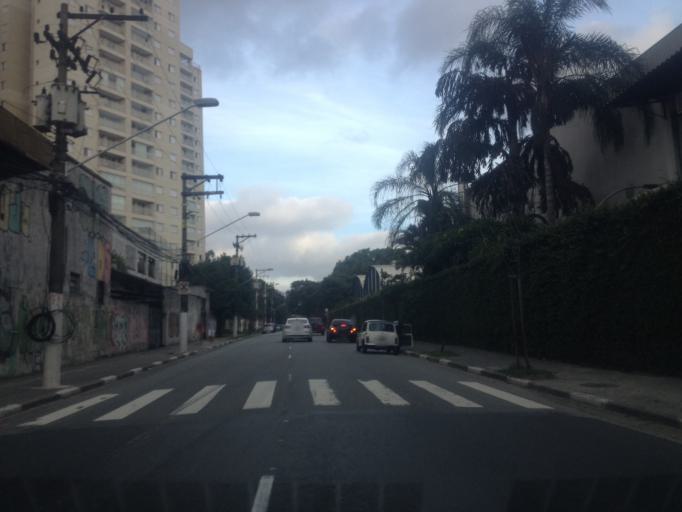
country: BR
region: Sao Paulo
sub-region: Diadema
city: Diadema
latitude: -23.6645
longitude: -46.7084
